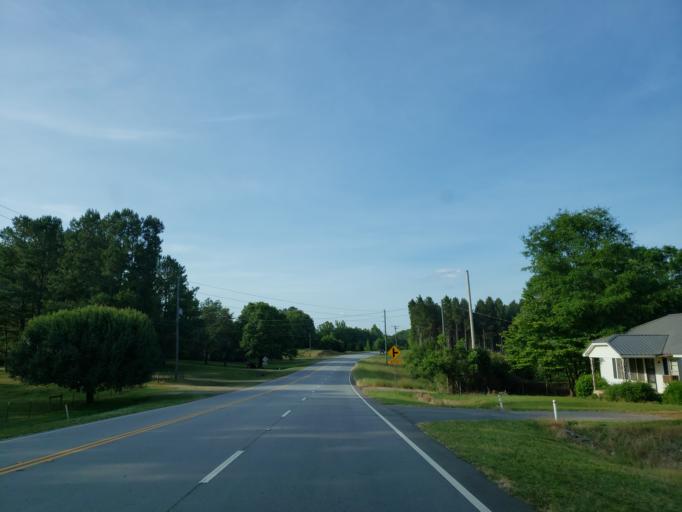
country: US
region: Georgia
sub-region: Carroll County
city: Bowdon
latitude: 33.5013
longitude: -85.2733
